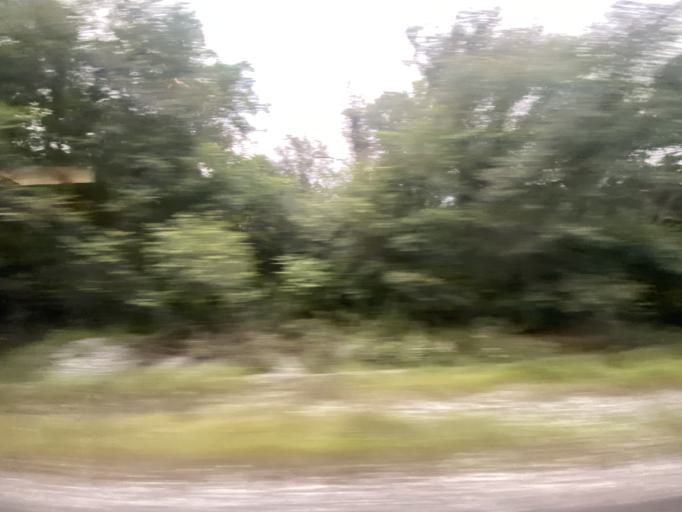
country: US
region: West Virginia
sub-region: Mineral County
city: Fort Ashby
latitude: 39.5326
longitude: -78.5940
